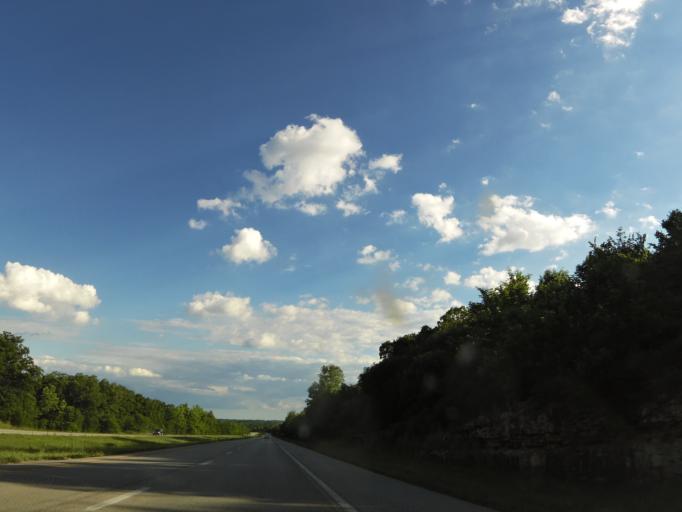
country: US
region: Missouri
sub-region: Lincoln County
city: Troy
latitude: 39.0330
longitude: -90.9782
